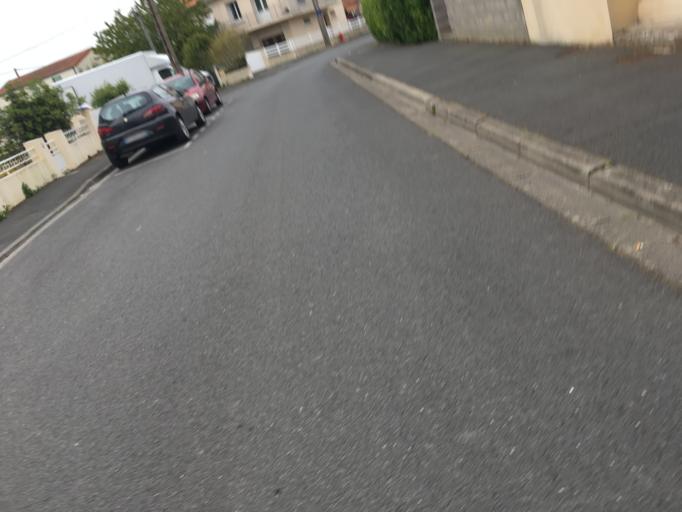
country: FR
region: Poitou-Charentes
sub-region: Departement de la Charente-Maritime
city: La Rochelle
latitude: 46.1671
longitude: -1.1306
